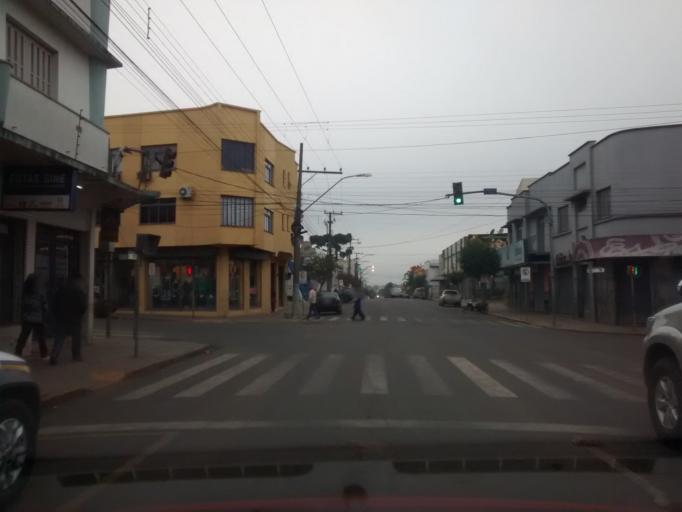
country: BR
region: Rio Grande do Sul
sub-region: Vacaria
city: Vacaria
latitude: -28.5050
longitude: -50.9377
